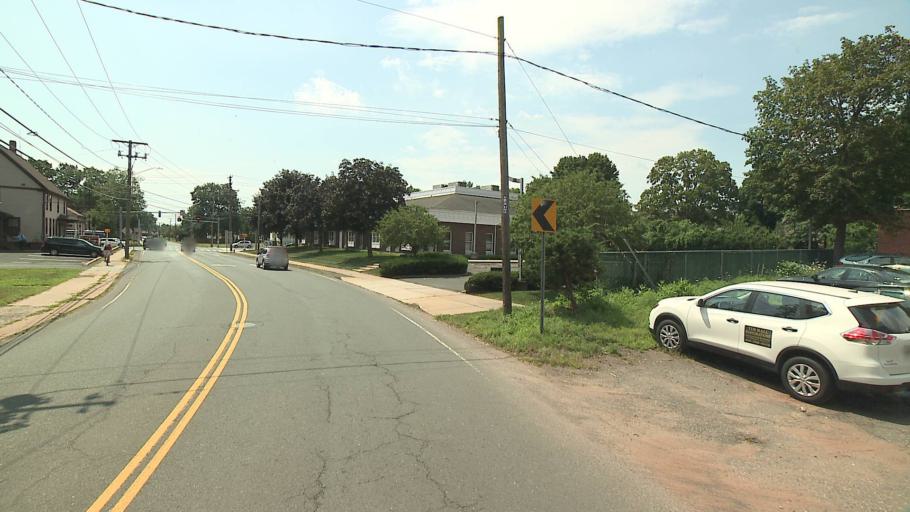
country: US
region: Connecticut
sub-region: Hartford County
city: Plainville
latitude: 41.6709
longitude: -72.8758
